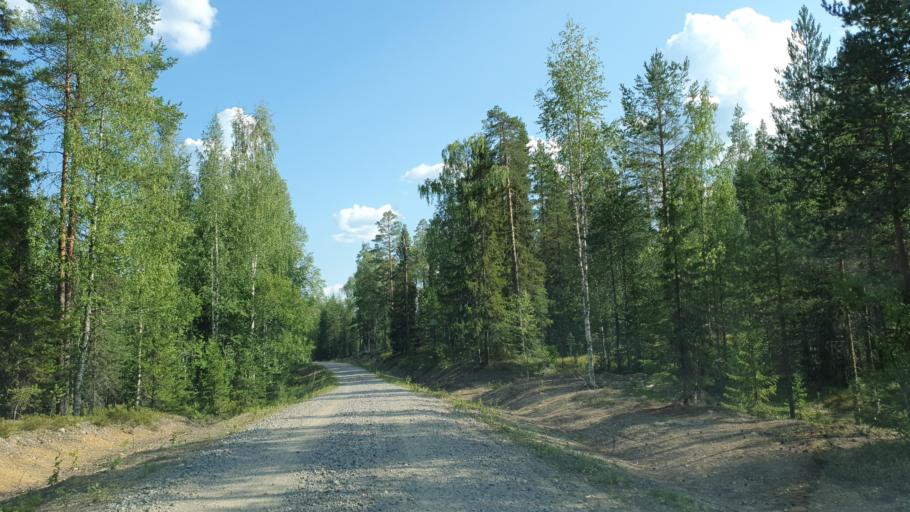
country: FI
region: Kainuu
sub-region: Kehys-Kainuu
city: Kuhmo
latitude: 63.9556
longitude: 29.5542
